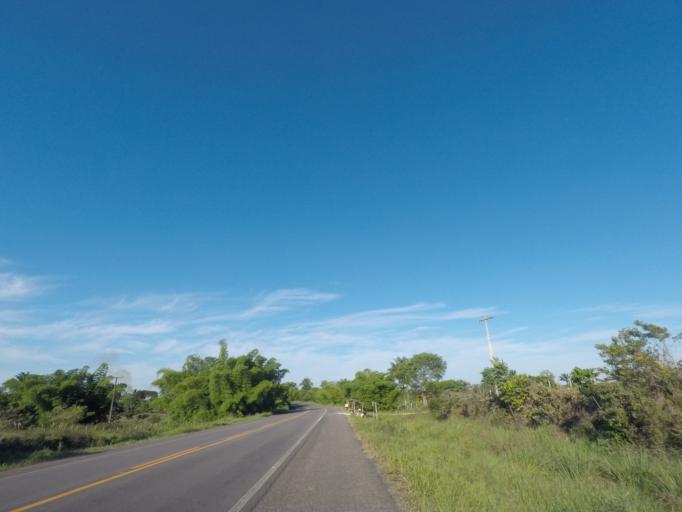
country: BR
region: Bahia
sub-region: Nazare
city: Nazare
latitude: -13.0050
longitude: -38.9659
